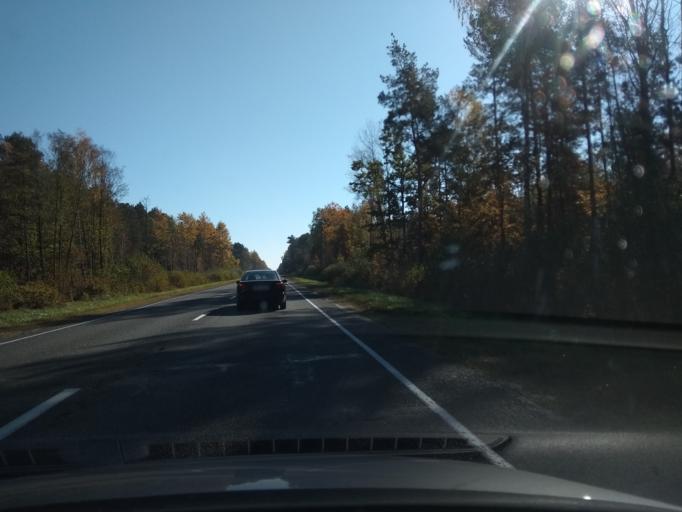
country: BY
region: Brest
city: Malaryta
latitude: 51.8981
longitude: 24.1279
